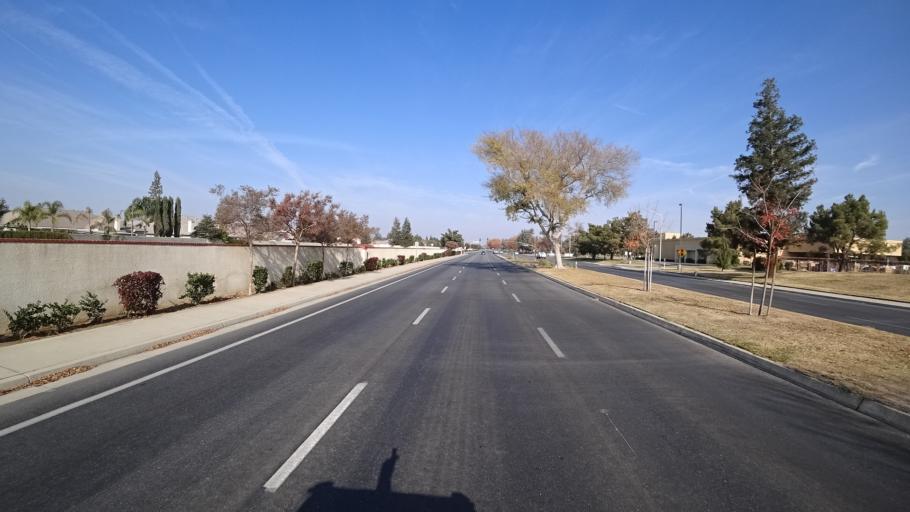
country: US
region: California
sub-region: Kern County
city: Greenacres
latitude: 35.3429
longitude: -119.1144
